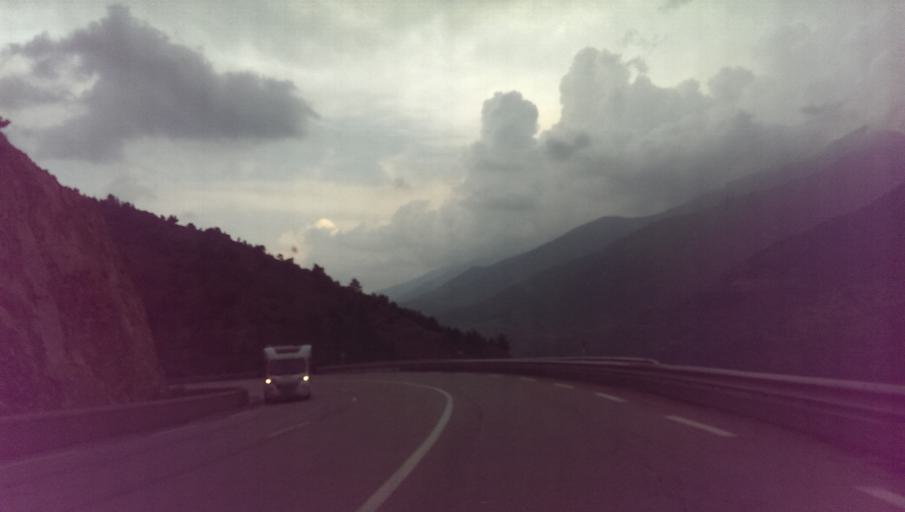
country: ES
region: Catalonia
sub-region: Provincia de Girona
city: Llivia
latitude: 42.5075
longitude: 2.1544
